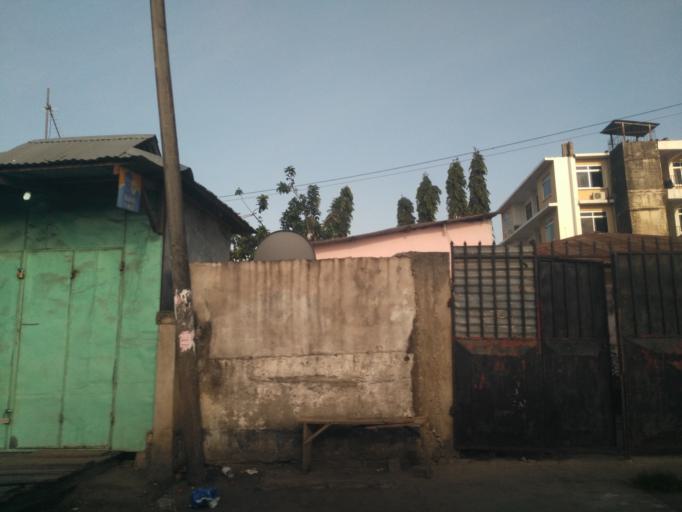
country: TZ
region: Dar es Salaam
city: Magomeni
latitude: -6.7851
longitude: 39.2657
